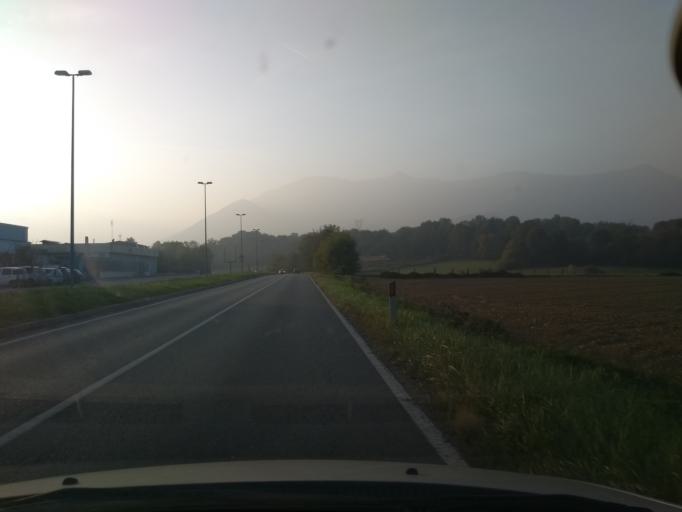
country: IT
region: Piedmont
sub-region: Provincia di Torino
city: San Gillio
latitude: 45.1519
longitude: 7.5256
